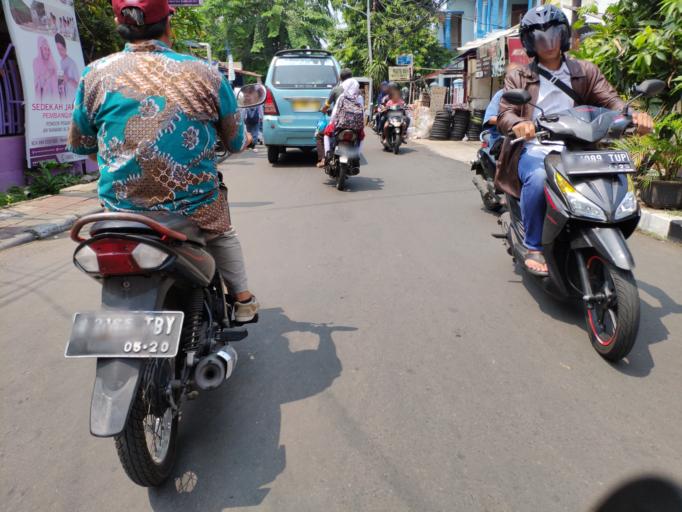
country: ID
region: Jakarta Raya
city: Jakarta
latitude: -6.2010
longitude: 106.8632
